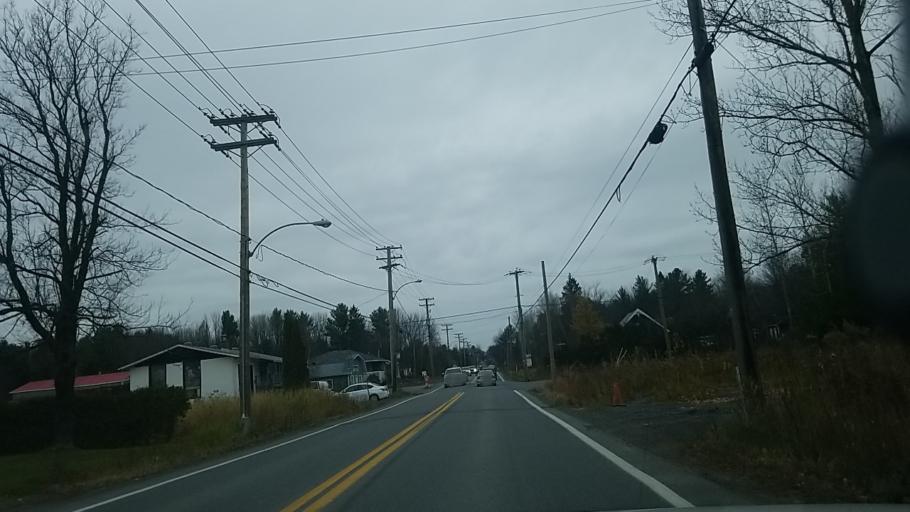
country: CA
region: Quebec
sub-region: Laurentides
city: Saint-Jerome
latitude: 45.7838
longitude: -74.0520
